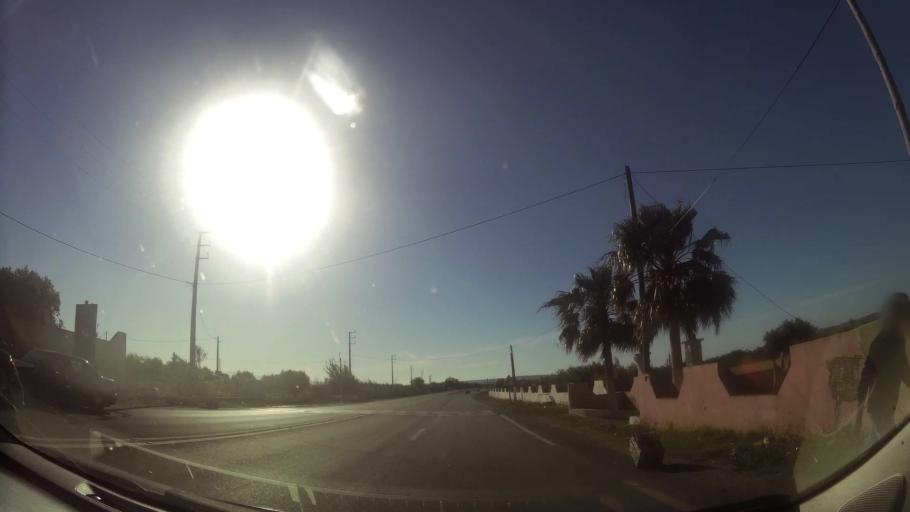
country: MA
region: Oriental
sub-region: Berkane-Taourirt
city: Ahfir
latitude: 35.0102
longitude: -2.1940
